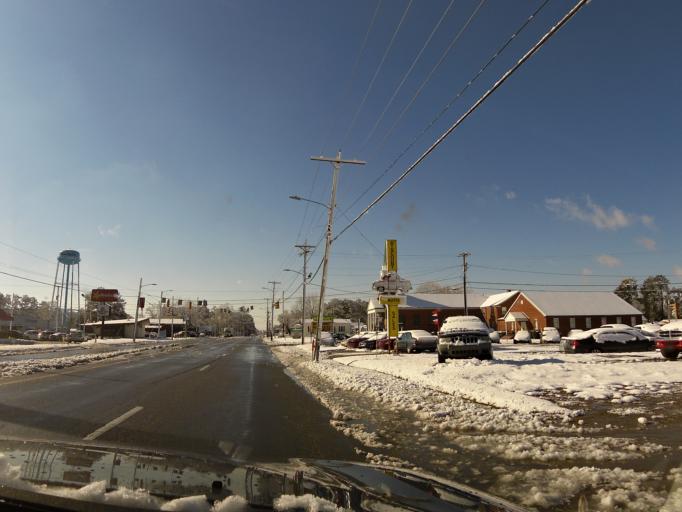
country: US
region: North Carolina
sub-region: Nash County
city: Sharpsburg
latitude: 35.8689
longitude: -77.8292
